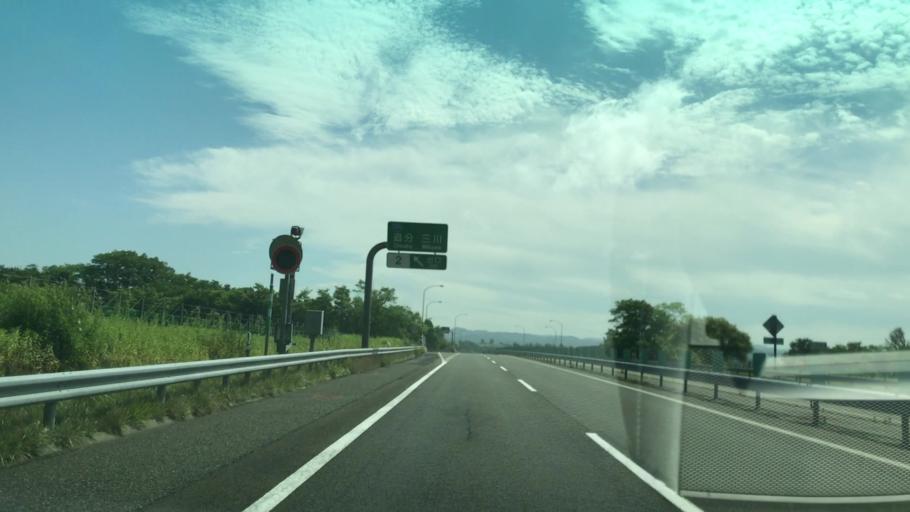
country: JP
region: Hokkaido
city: Chitose
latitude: 42.8932
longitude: 141.8077
